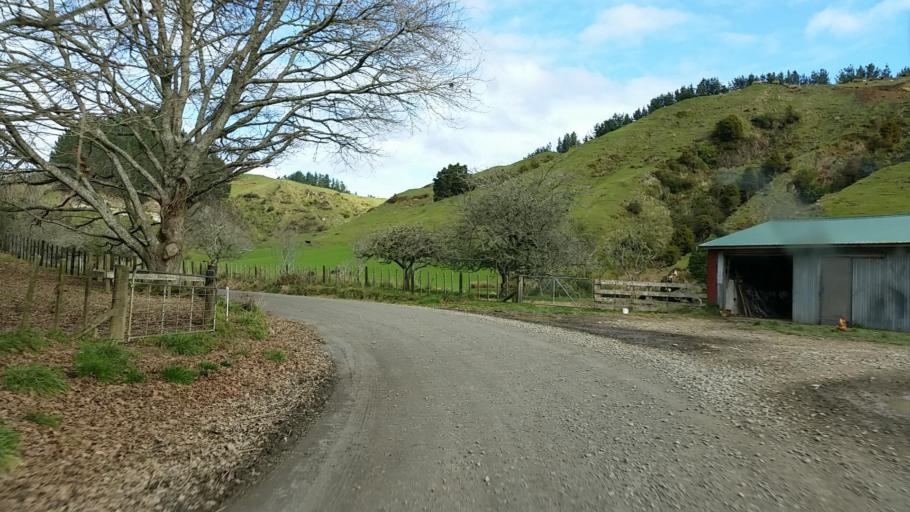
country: NZ
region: Taranaki
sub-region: New Plymouth District
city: Waitara
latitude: -39.1391
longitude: 174.5683
